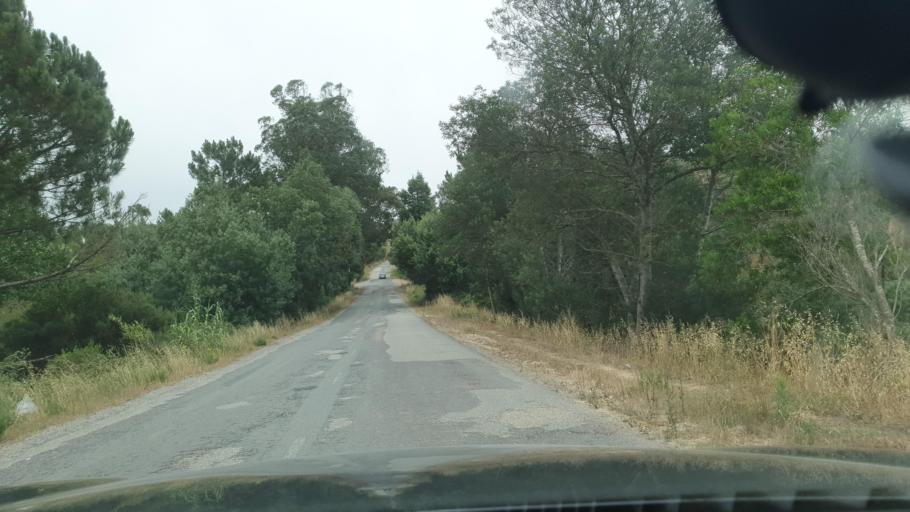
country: PT
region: Beja
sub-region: Odemira
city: Sao Teotonio
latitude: 37.5120
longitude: -8.7004
